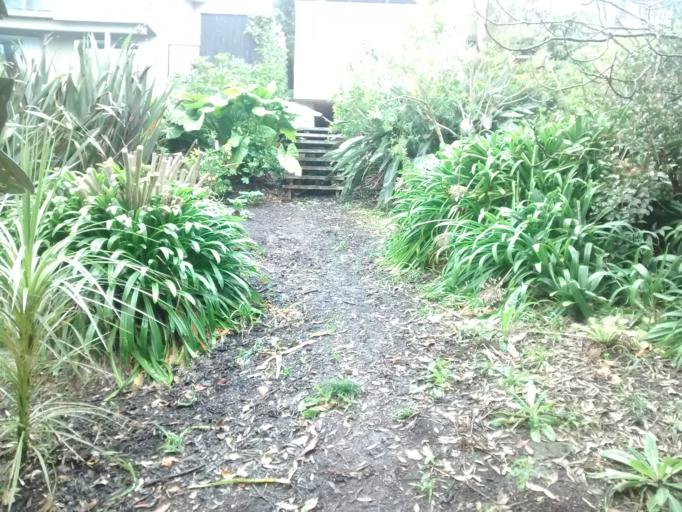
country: NZ
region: Auckland
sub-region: Auckland
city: Rosebank
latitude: -36.8538
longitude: 174.7138
